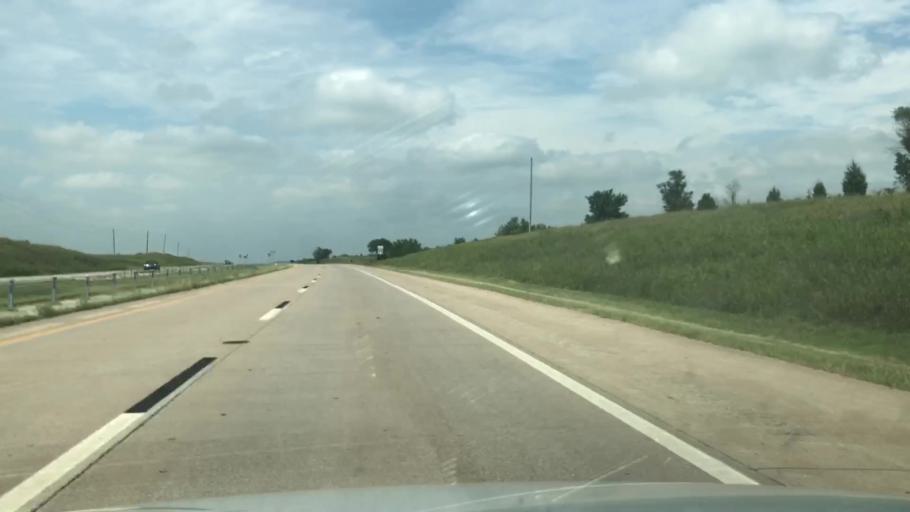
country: US
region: Oklahoma
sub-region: Osage County
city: Skiatook
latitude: 36.5113
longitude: -95.9211
